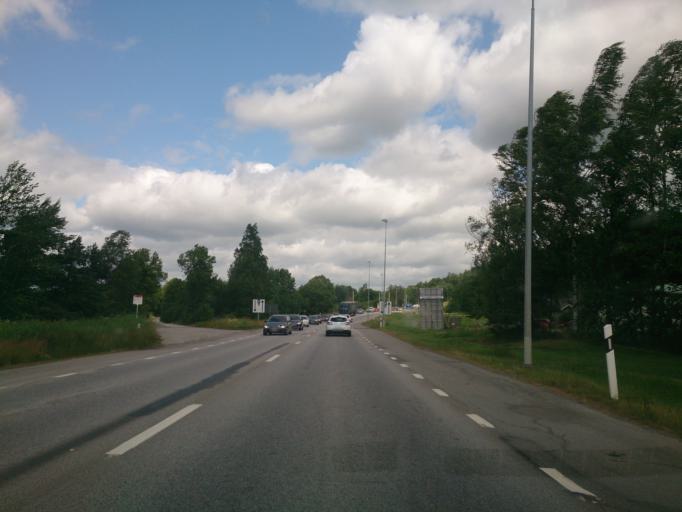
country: SE
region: OEstergoetland
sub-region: Soderkopings Kommun
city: Soederkoeping
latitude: 58.4866
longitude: 16.3106
